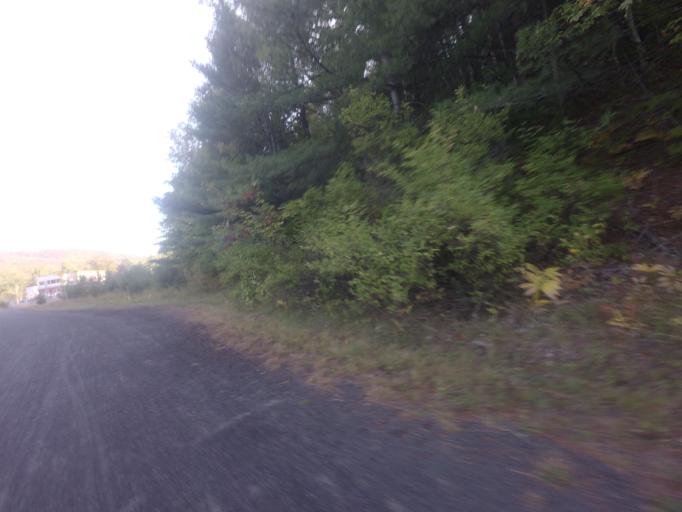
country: CA
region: Quebec
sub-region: Laurentides
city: Sainte-Adele
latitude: 45.9883
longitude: -74.1184
